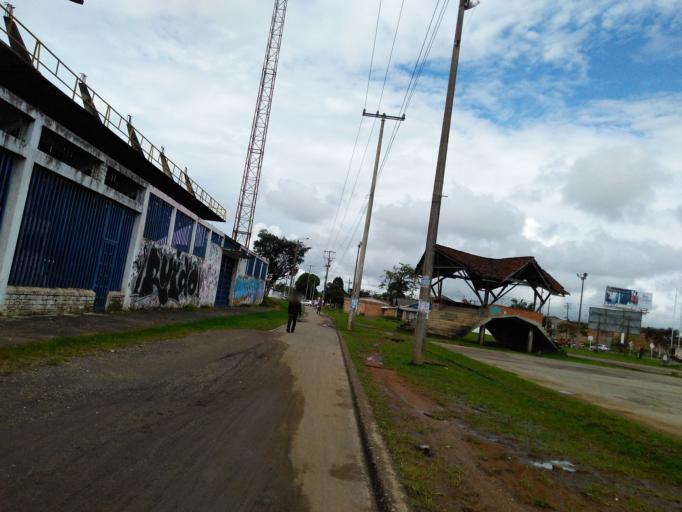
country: CO
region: Cauca
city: Popayan
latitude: 2.4549
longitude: -76.5918
